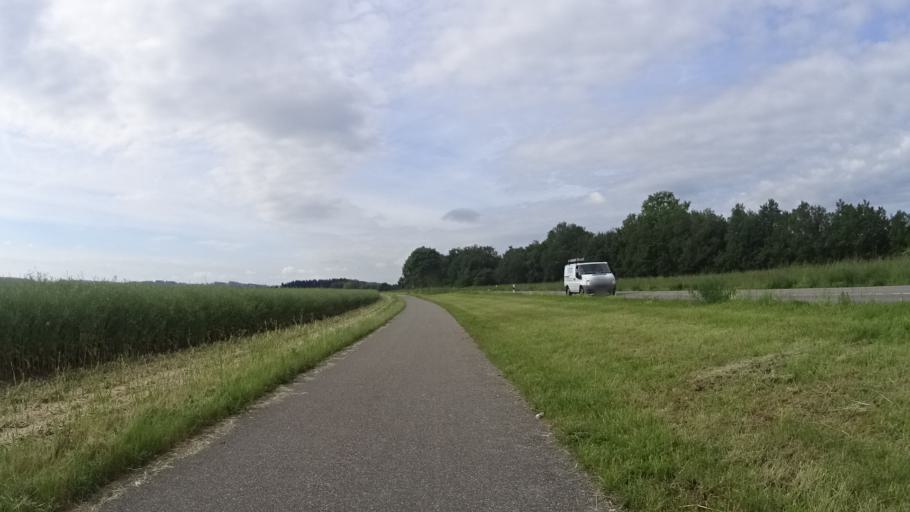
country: DE
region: Baden-Wuerttemberg
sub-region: Freiburg Region
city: Neuenburg am Rhein
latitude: 47.7943
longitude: 7.5559
